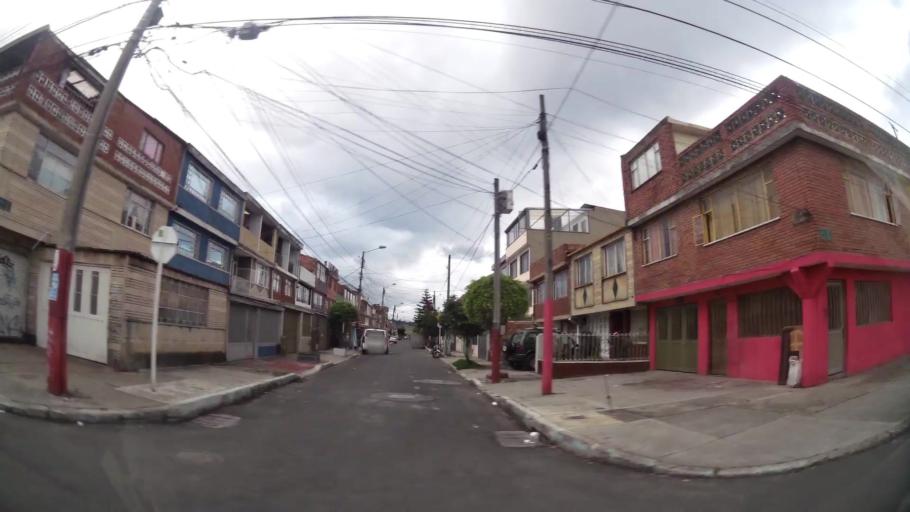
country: CO
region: Bogota D.C.
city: Bogota
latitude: 4.6909
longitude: -74.1060
